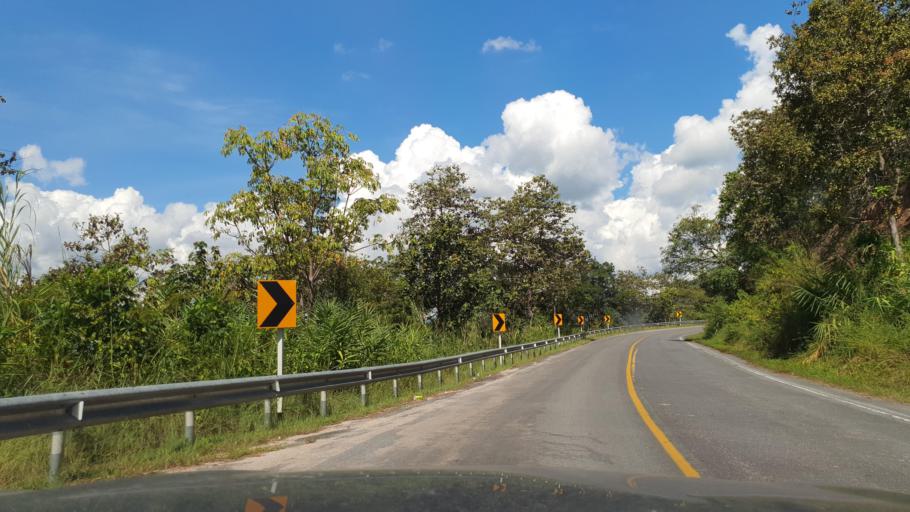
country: TH
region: Chiang Mai
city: Phrao
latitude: 19.3700
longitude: 99.2467
